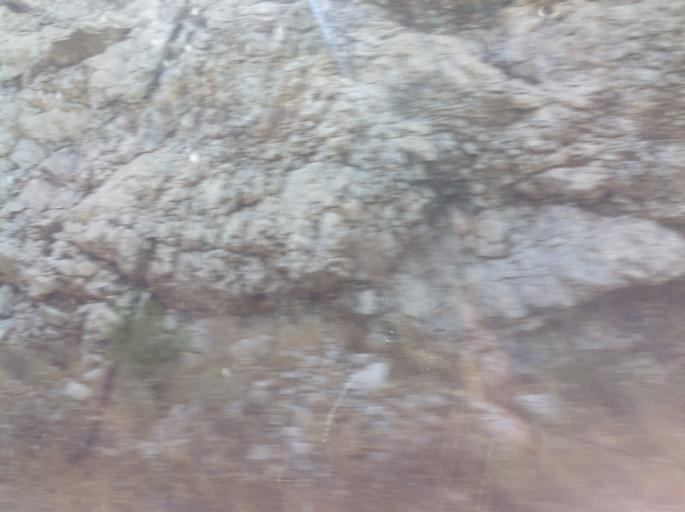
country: GR
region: Attica
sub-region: Nomos Attikis
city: Zografos
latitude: 37.9664
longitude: 23.7896
